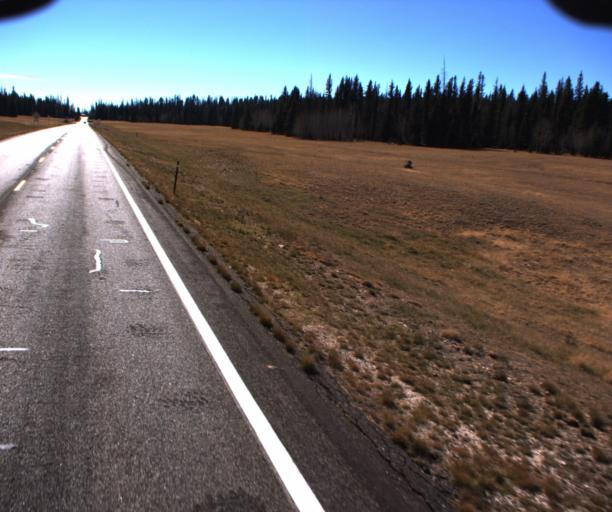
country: US
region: Arizona
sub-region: Coconino County
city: Grand Canyon
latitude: 36.3433
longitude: -112.1172
